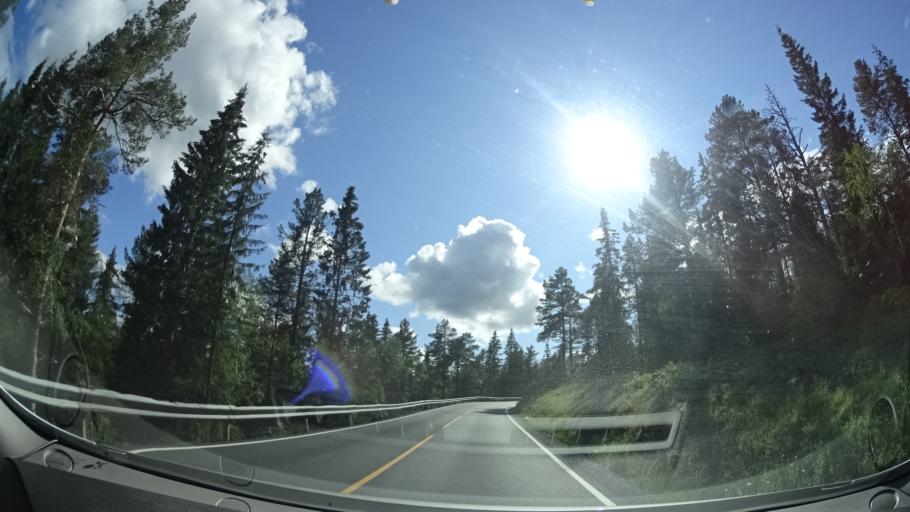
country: NO
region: Sor-Trondelag
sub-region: Snillfjord
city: Krokstadora
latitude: 63.2299
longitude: 9.5767
